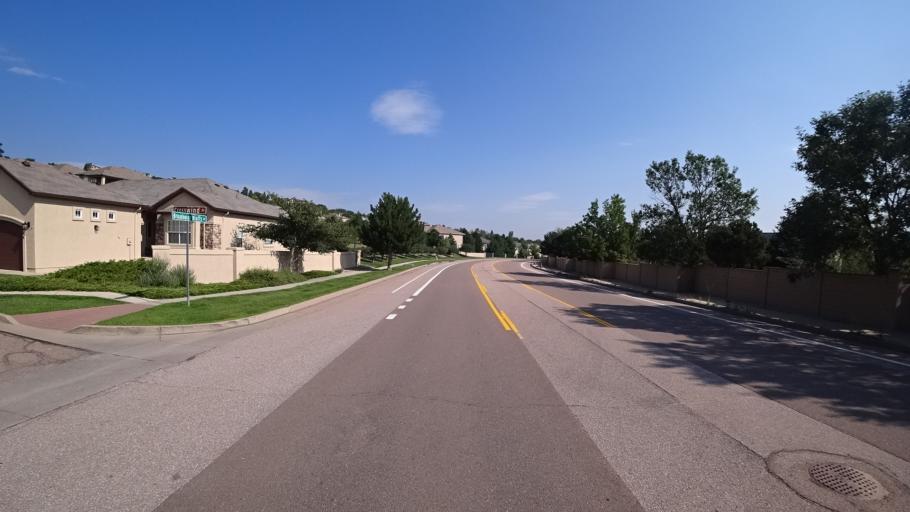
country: US
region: Colorado
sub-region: El Paso County
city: Fort Carson
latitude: 38.7634
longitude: -104.8186
